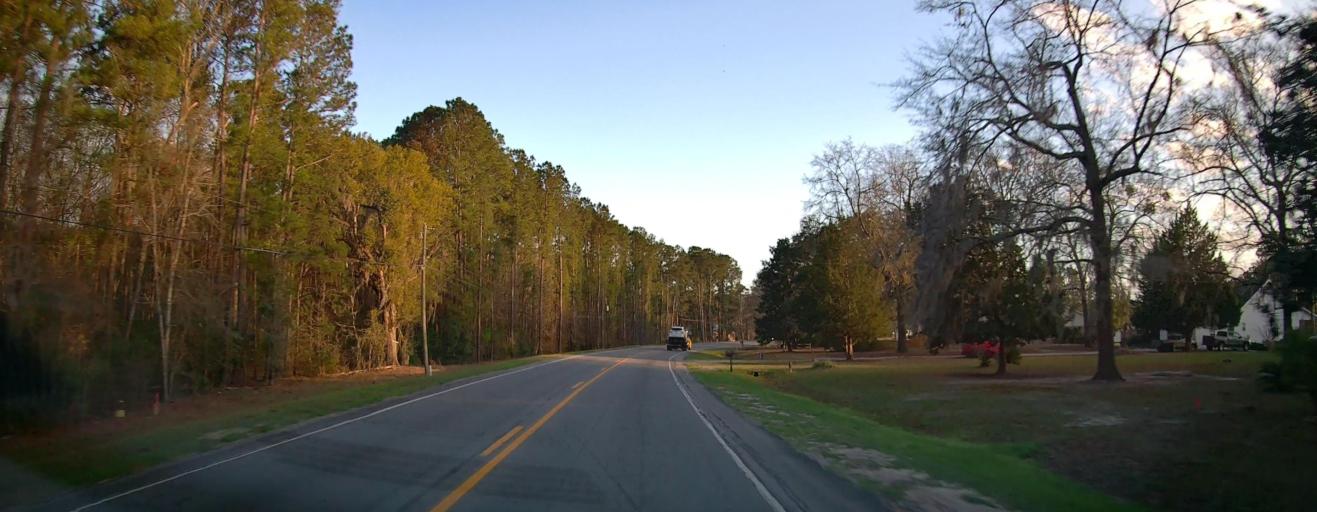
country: US
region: Georgia
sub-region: Chatham County
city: Bloomingdale
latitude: 32.1665
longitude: -81.3854
